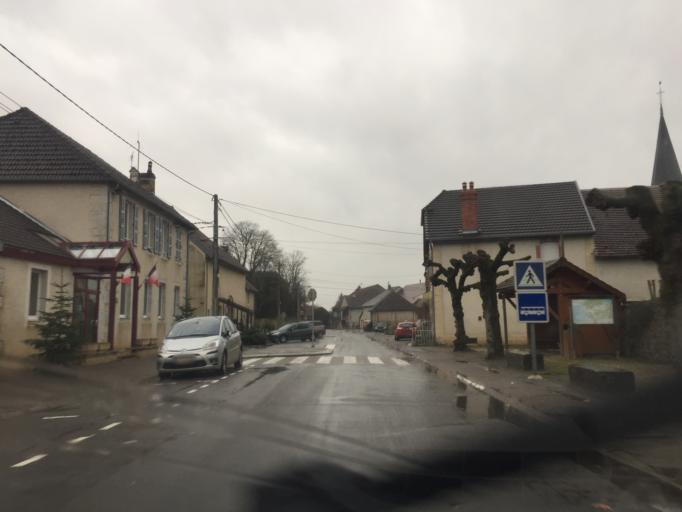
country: FR
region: Franche-Comte
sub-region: Departement du Doubs
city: Arc-et-Senans
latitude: 47.0120
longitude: 5.7773
